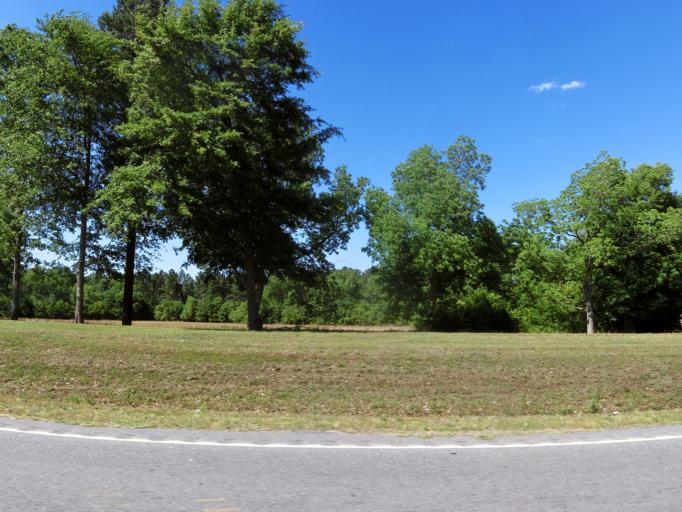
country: US
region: South Carolina
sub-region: Barnwell County
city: Williston
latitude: 33.3797
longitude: -81.3758
